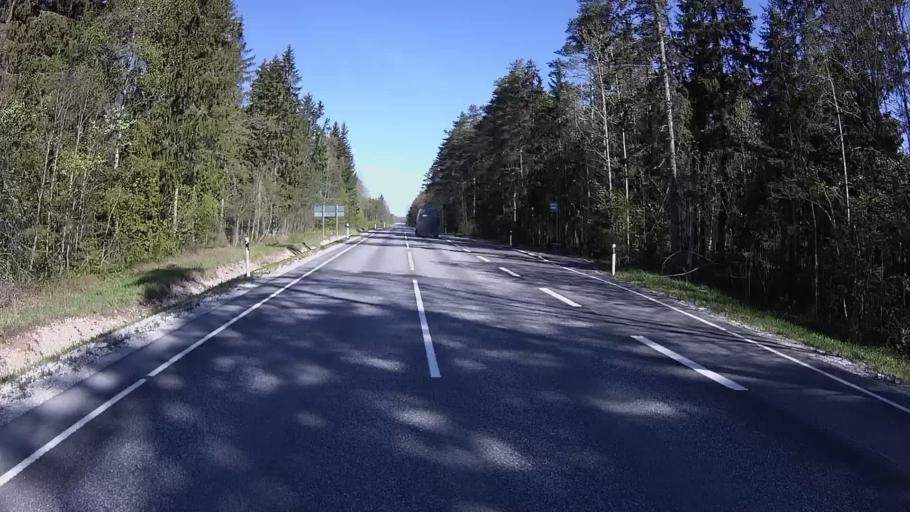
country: EE
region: Raplamaa
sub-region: Jaervakandi vald
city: Jarvakandi
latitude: 58.8609
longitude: 24.7887
